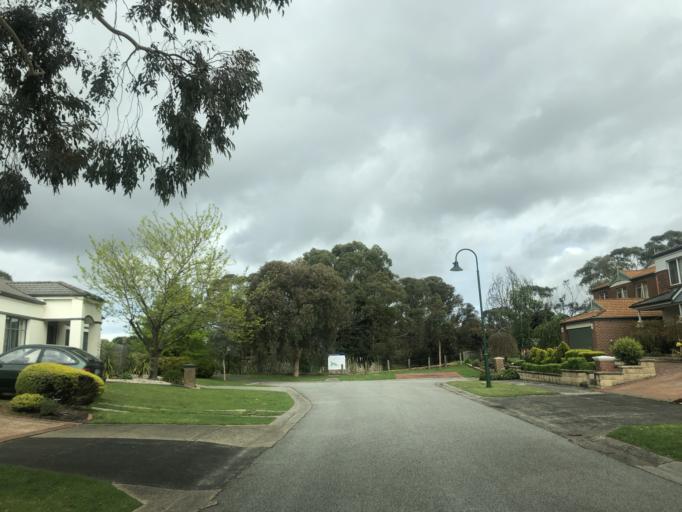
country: AU
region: Victoria
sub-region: Knox
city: Rowville
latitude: -37.9401
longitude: 145.2257
